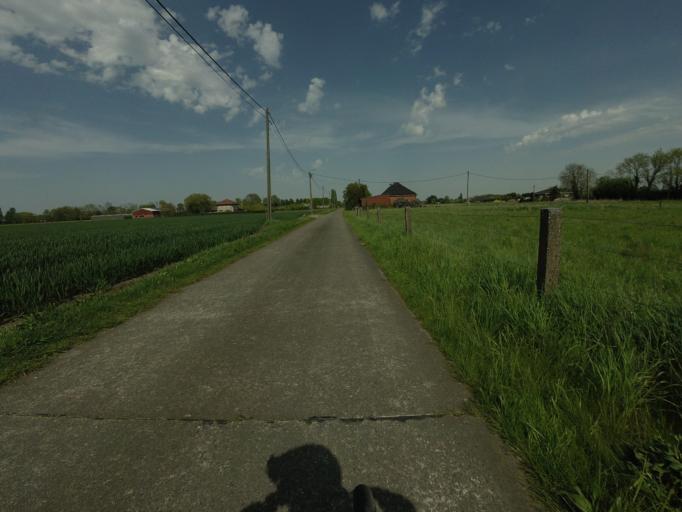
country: BE
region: Flanders
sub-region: Provincie Antwerpen
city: Putte
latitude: 51.0655
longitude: 4.6135
